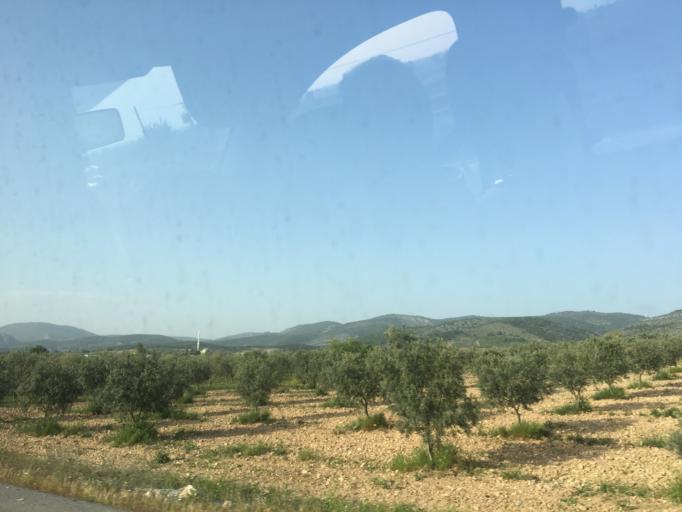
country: TR
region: Manisa
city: Golmarmara
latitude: 38.7875
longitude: 27.9034
